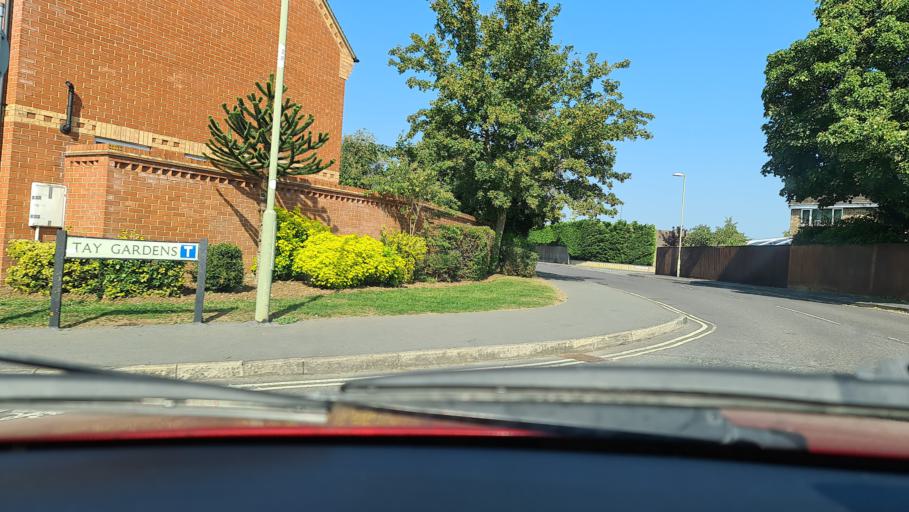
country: GB
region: England
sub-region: Oxfordshire
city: Bicester
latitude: 51.9045
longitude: -1.1712
